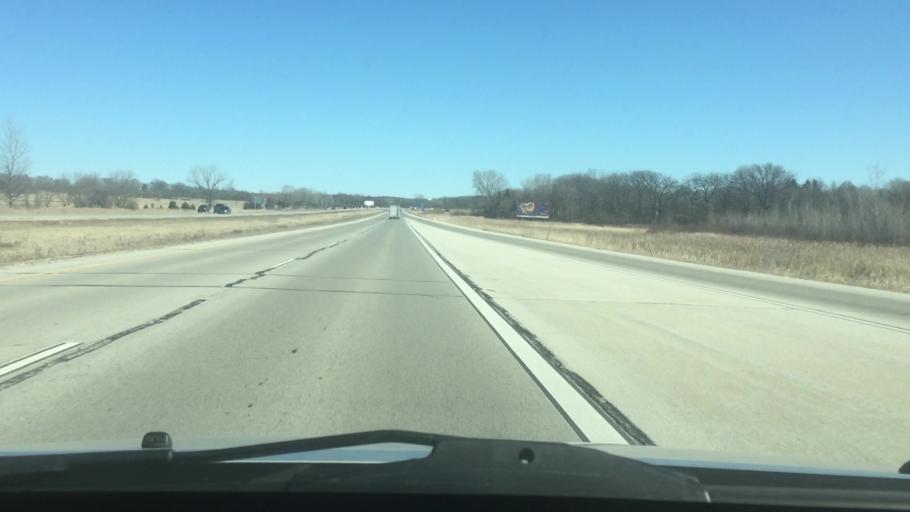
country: US
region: Wisconsin
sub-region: Waukesha County
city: Pewaukee
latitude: 43.0937
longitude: -88.2682
